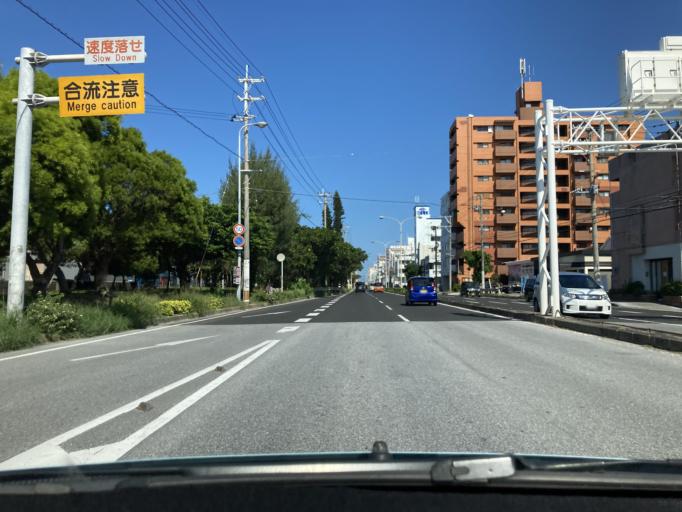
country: JP
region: Okinawa
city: Naha-shi
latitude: 26.2323
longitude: 127.6816
